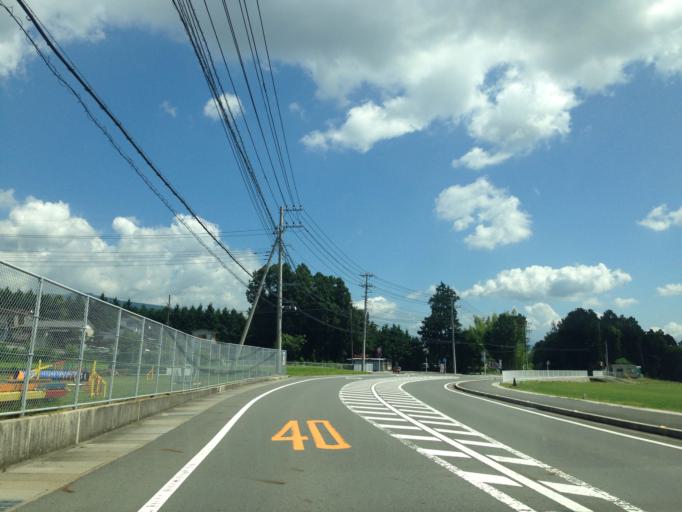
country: JP
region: Shizuoka
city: Gotemba
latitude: 35.2163
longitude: 138.8957
